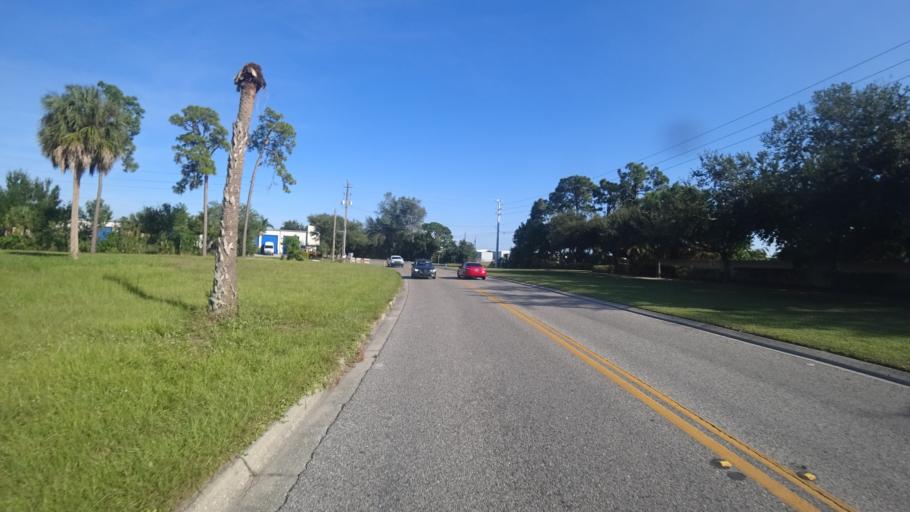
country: US
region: Florida
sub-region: Manatee County
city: Whitfield
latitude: 27.4040
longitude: -82.5522
